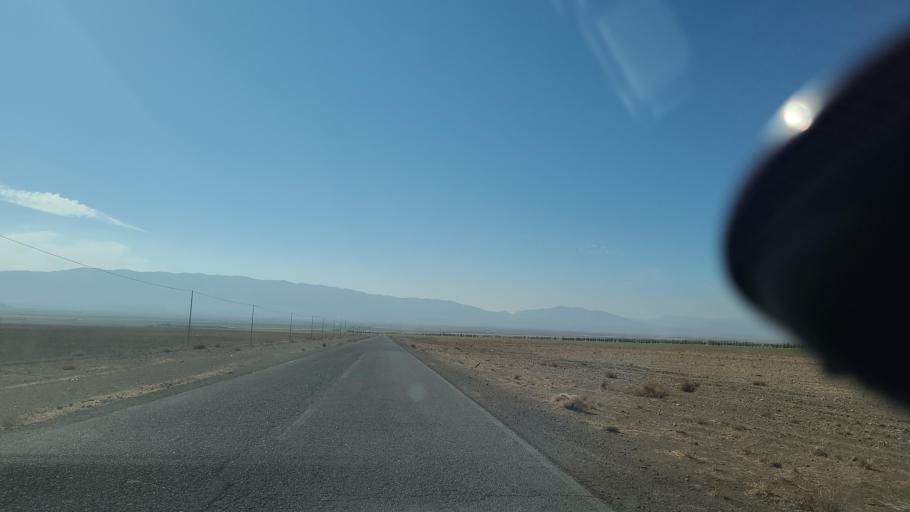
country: IR
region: Razavi Khorasan
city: Dowlatabad
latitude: 35.6136
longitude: 59.4722
